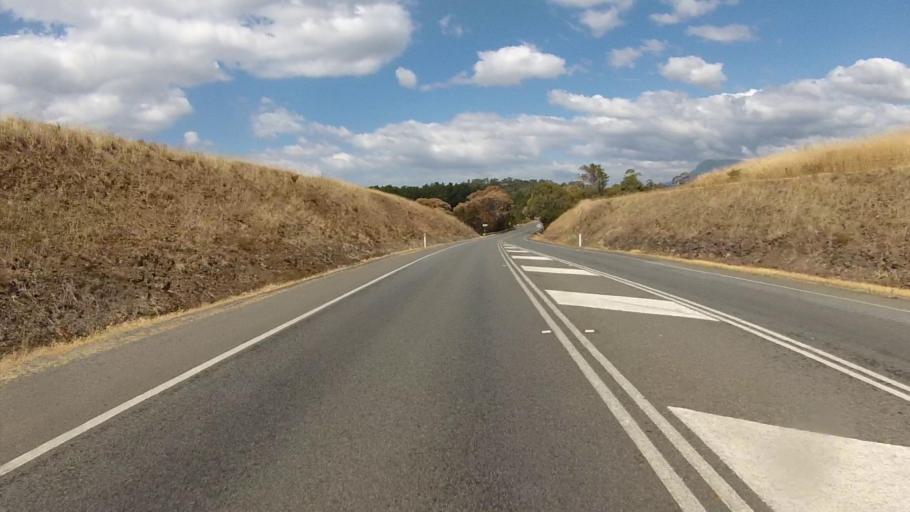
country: AU
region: Tasmania
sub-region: Brighton
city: Old Beach
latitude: -42.7635
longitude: 147.2696
